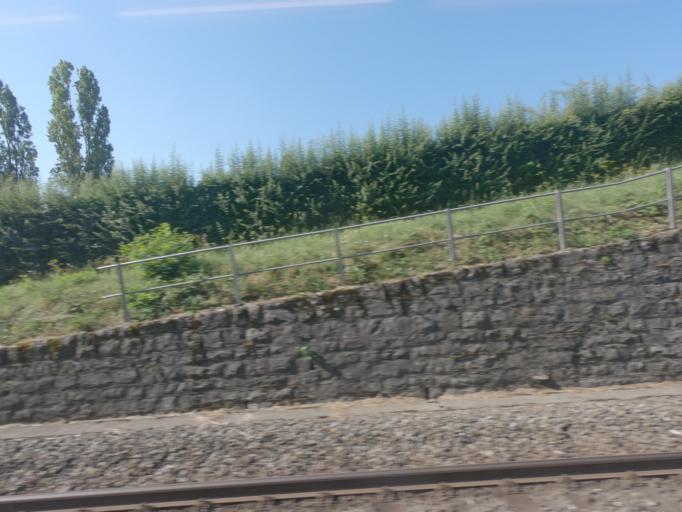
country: CH
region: Vaud
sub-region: Riviera-Pays-d'Enhaut District
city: La Tour-de-Peilz
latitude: 46.4484
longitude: 6.8753
